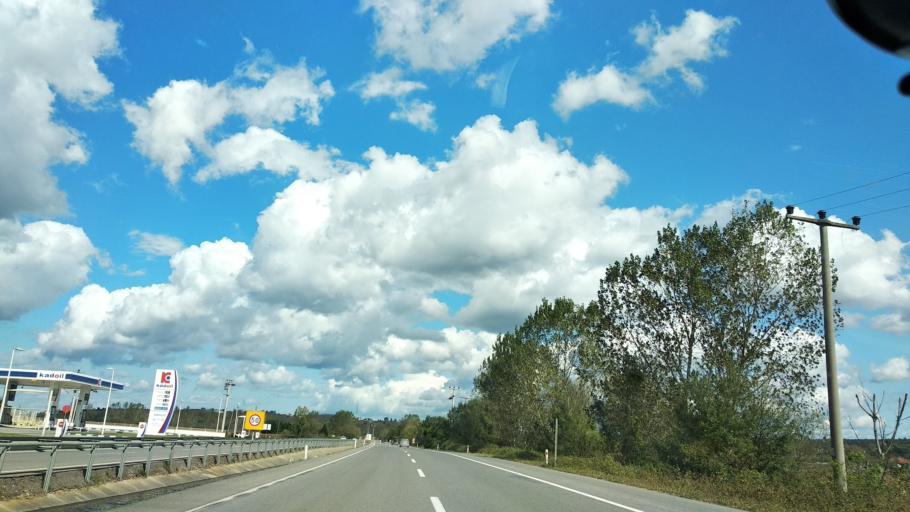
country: TR
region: Sakarya
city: Ferizli
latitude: 40.9834
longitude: 30.5434
